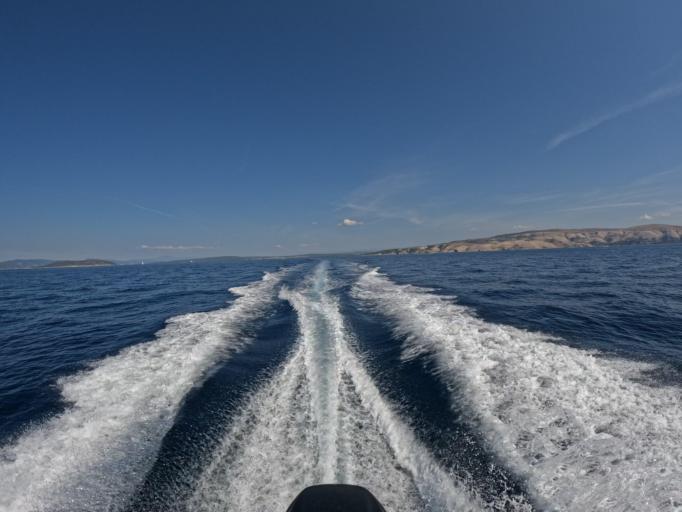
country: HR
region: Primorsko-Goranska
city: Punat
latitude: 44.9231
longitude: 14.6205
